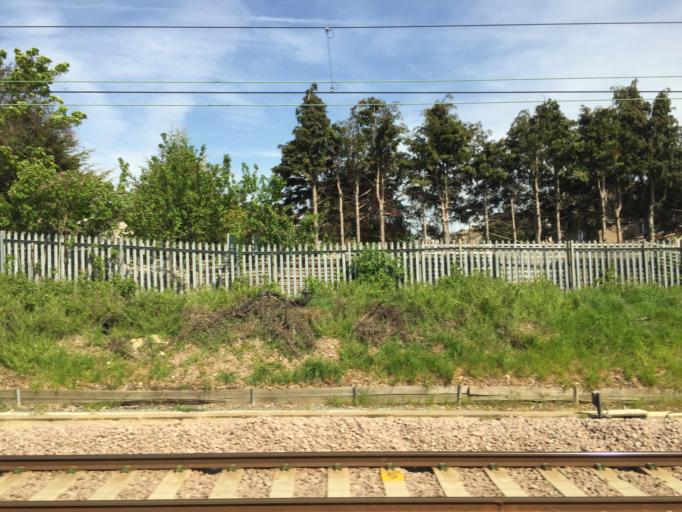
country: GB
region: England
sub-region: Greater London
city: Chadwell Heath
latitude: 51.5683
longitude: 0.1321
